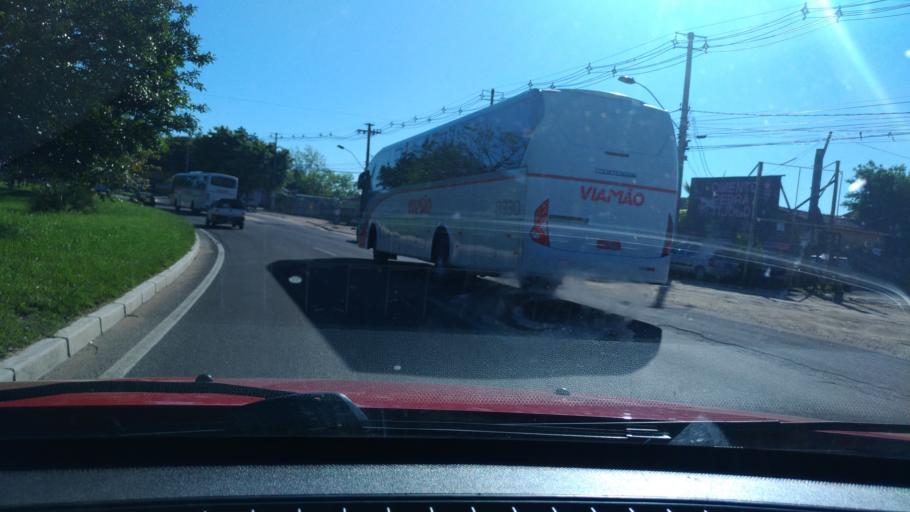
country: BR
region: Rio Grande do Sul
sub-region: Viamao
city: Viamao
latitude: -30.0922
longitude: -51.0639
